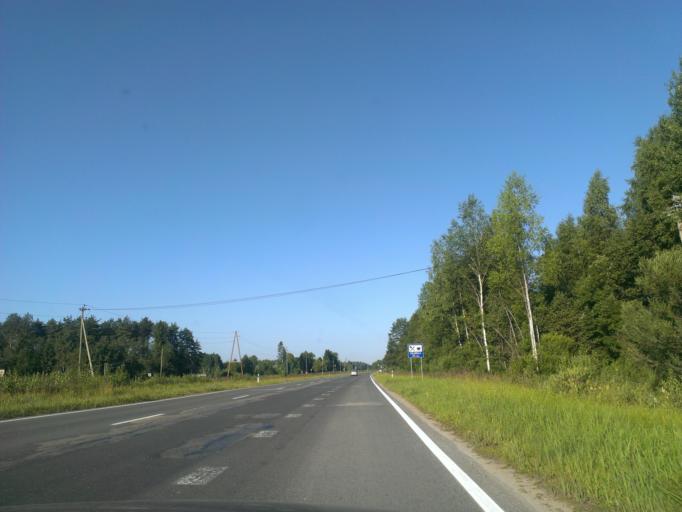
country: LV
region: Incukalns
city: Vangazi
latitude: 57.0925
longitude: 24.5608
